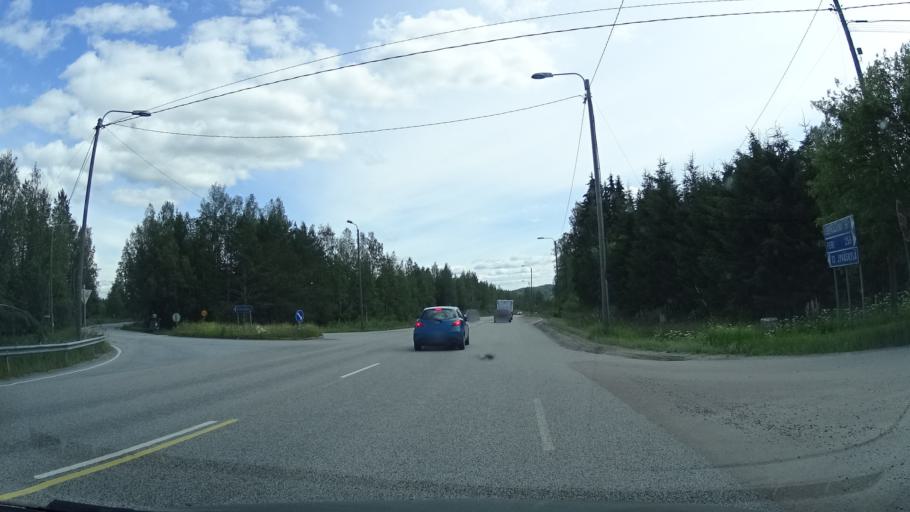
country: FI
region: Central Finland
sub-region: Jyvaeskylae
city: Jyvaeskylae
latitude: 62.2603
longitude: 25.5997
